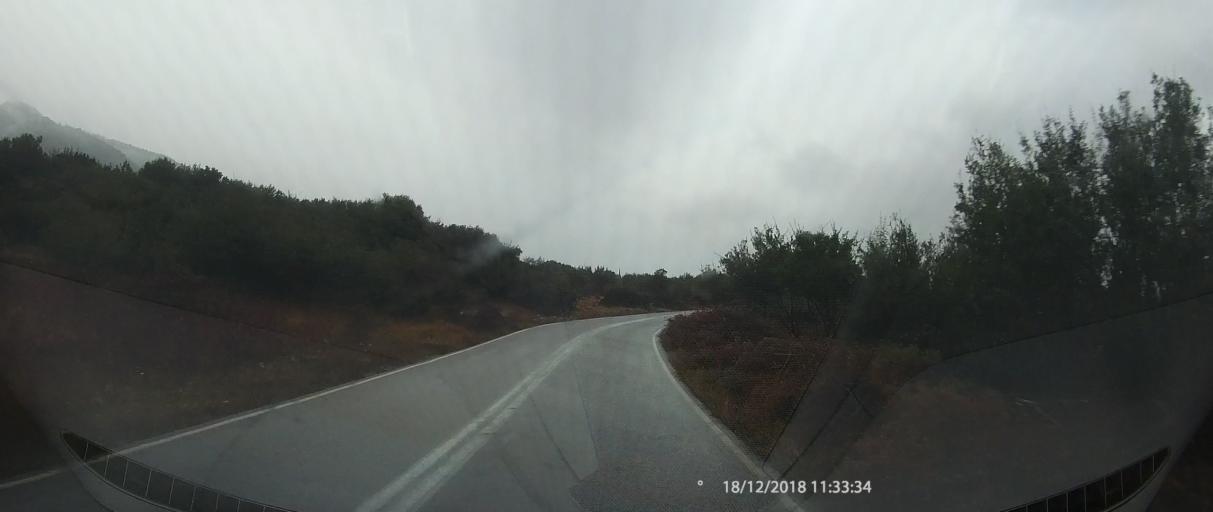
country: GR
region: Central Macedonia
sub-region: Nomos Pierias
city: Litochoro
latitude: 40.1118
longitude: 22.4929
